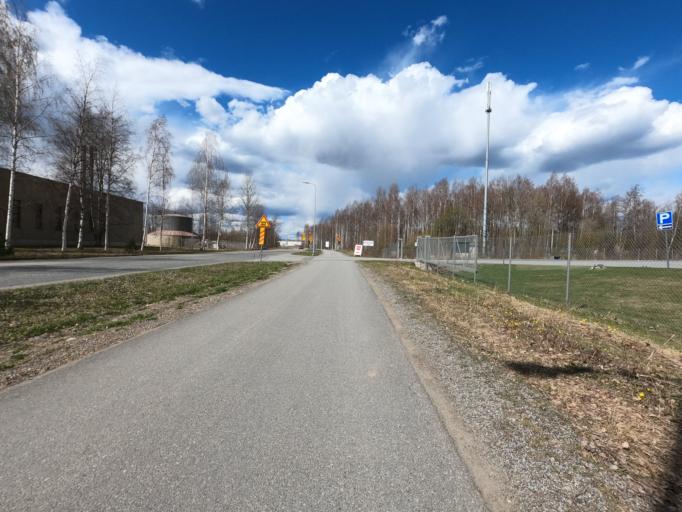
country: FI
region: North Karelia
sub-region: Joensuu
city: Joensuu
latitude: 62.5851
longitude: 29.7588
